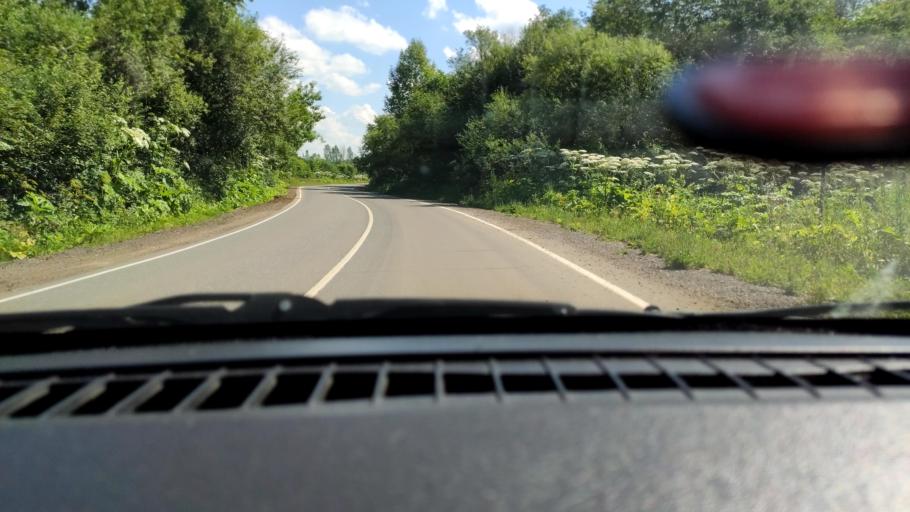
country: RU
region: Perm
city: Yugo-Kamskiy
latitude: 57.6900
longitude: 55.4989
